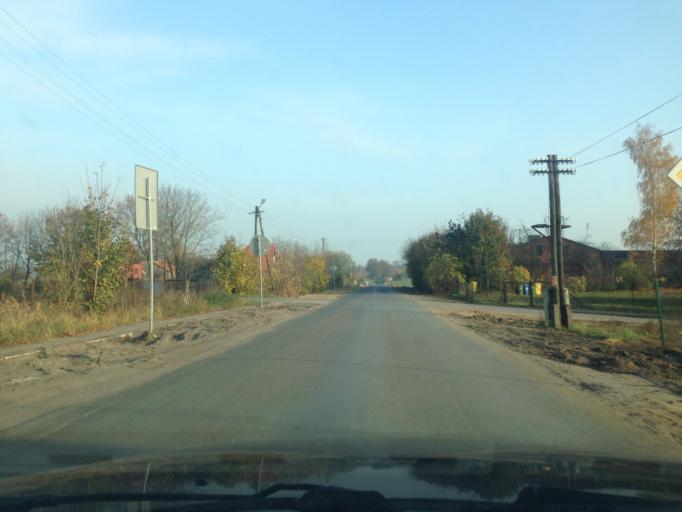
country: PL
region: Kujawsko-Pomorskie
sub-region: Powiat wabrzeski
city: Debowa Laka
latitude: 53.2569
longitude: 19.0975
